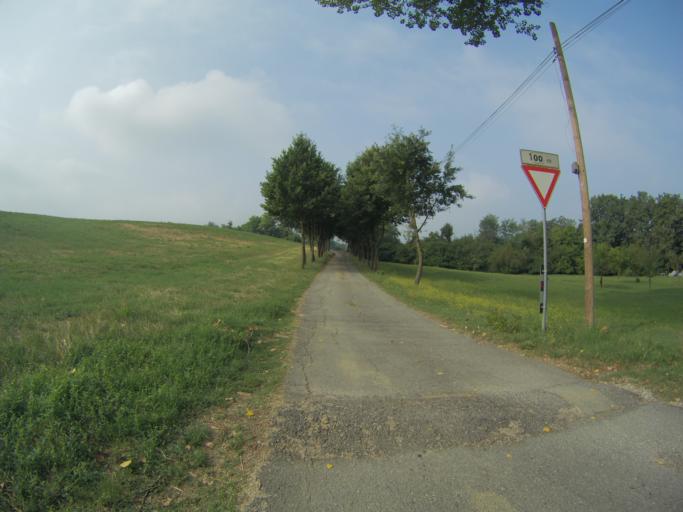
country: IT
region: Emilia-Romagna
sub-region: Provincia di Reggio Emilia
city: Albinea
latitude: 44.6178
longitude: 10.6214
